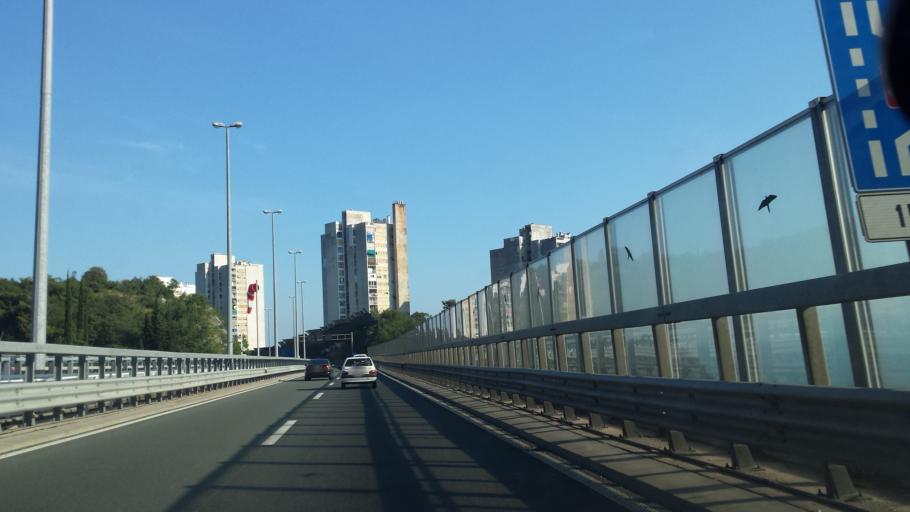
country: HR
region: Primorsko-Goranska
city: Drenova
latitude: 45.3419
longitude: 14.4304
